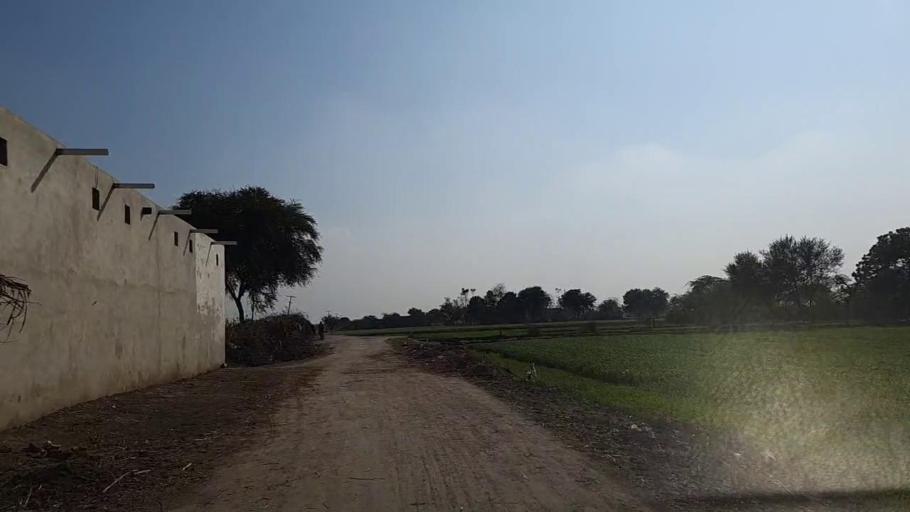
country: PK
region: Sindh
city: Jam Sahib
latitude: 26.2771
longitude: 68.6109
